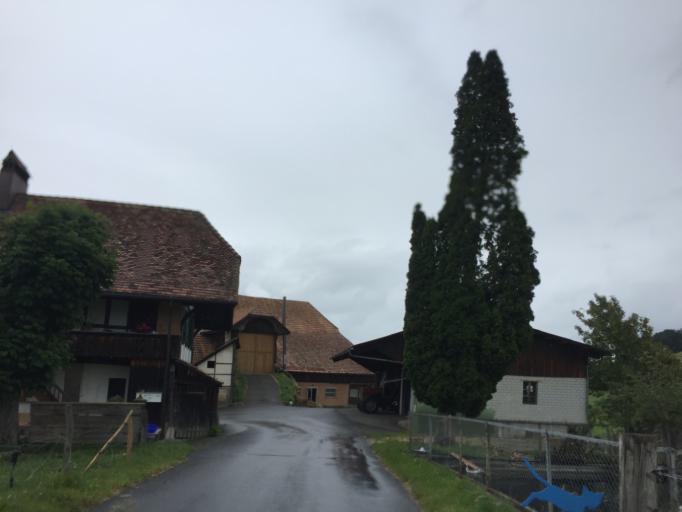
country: CH
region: Bern
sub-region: Bern-Mittelland District
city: Taegertschi
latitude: 46.8902
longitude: 7.5926
